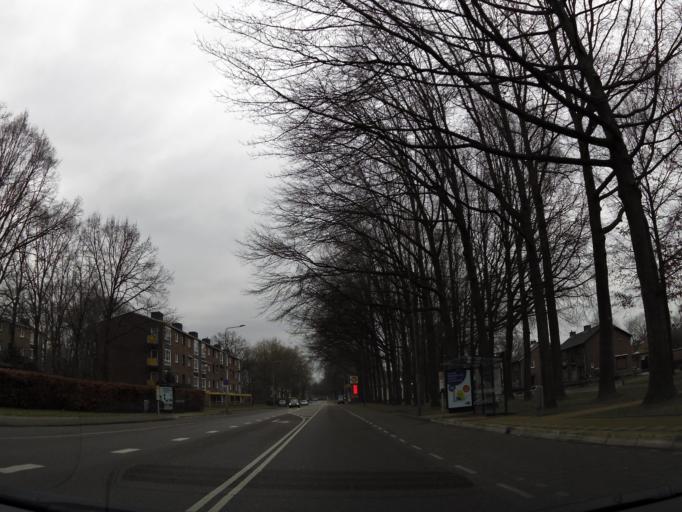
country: NL
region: Limburg
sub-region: Gemeente Sittard-Geleen
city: Sittard
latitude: 51.0051
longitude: 5.8713
